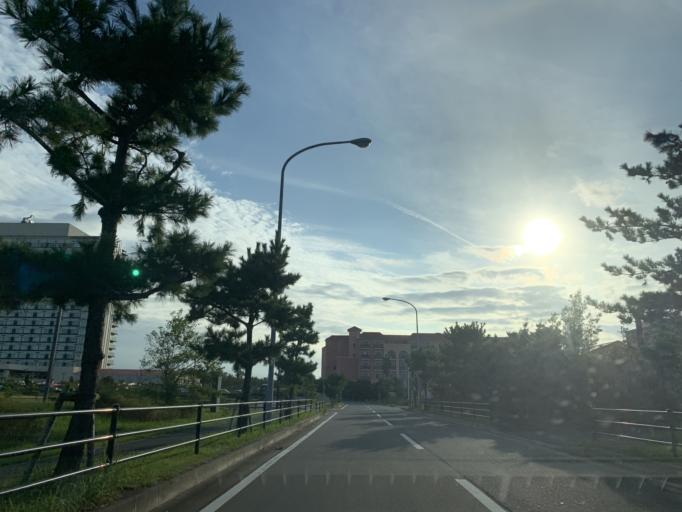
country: JP
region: Tokyo
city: Urayasu
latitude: 35.6398
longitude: 139.9322
